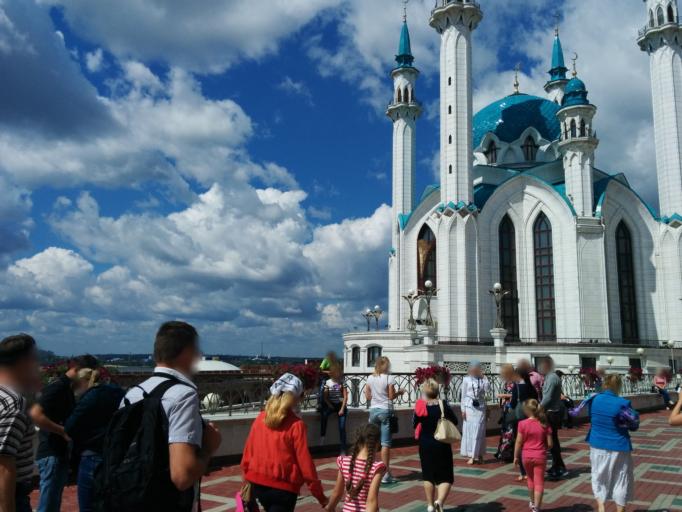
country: RU
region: Tatarstan
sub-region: Gorod Kazan'
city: Kazan
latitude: 55.7979
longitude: 49.1062
